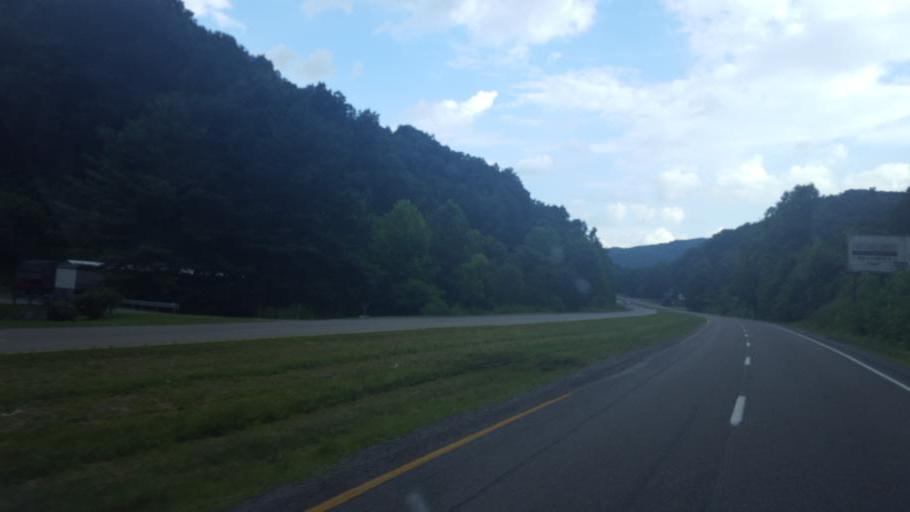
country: US
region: Virginia
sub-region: Wise County
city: Wise
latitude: 37.0456
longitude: -82.6003
